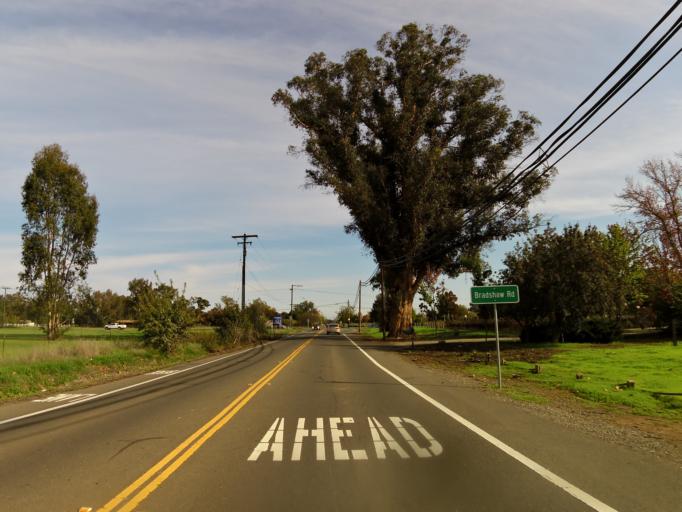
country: US
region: California
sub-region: Sacramento County
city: Elk Grove
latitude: 38.4091
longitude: -121.3363
